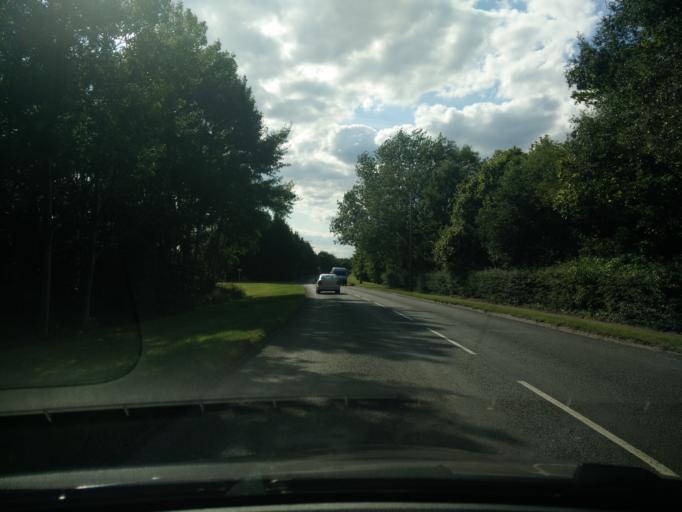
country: GB
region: England
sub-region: Derbyshire
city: Ilkeston
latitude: 52.9462
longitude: -1.3037
